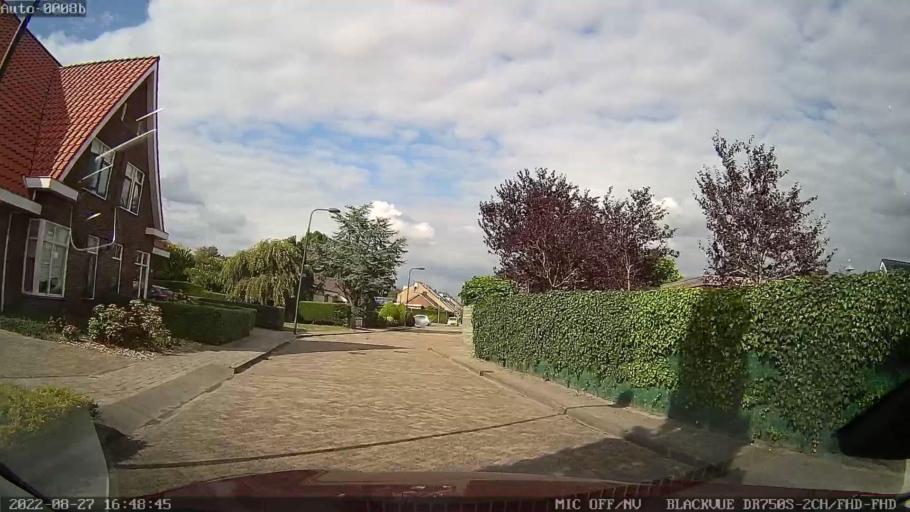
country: NL
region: South Holland
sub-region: Gemeente Goeree-Overflakkee
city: Ouddorp
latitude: 51.7113
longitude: 3.9477
